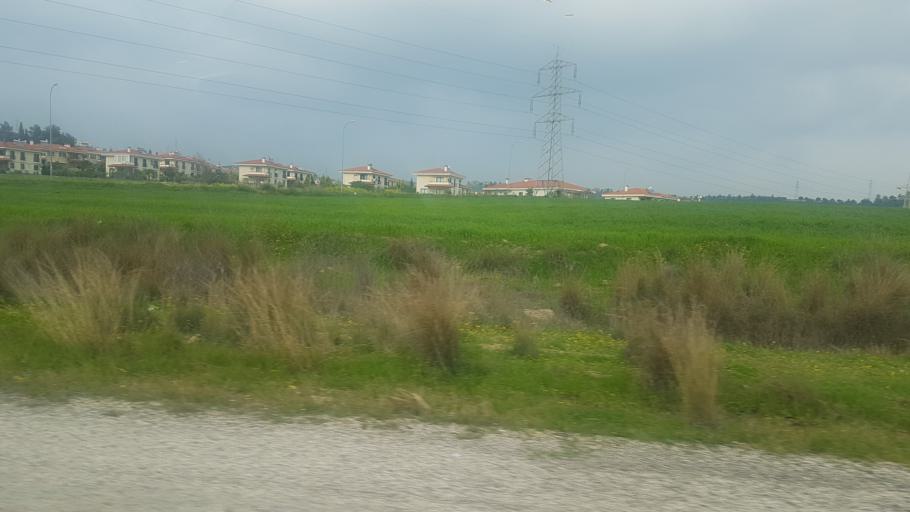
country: TR
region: Mersin
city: Yenice
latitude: 37.0504
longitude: 35.1753
